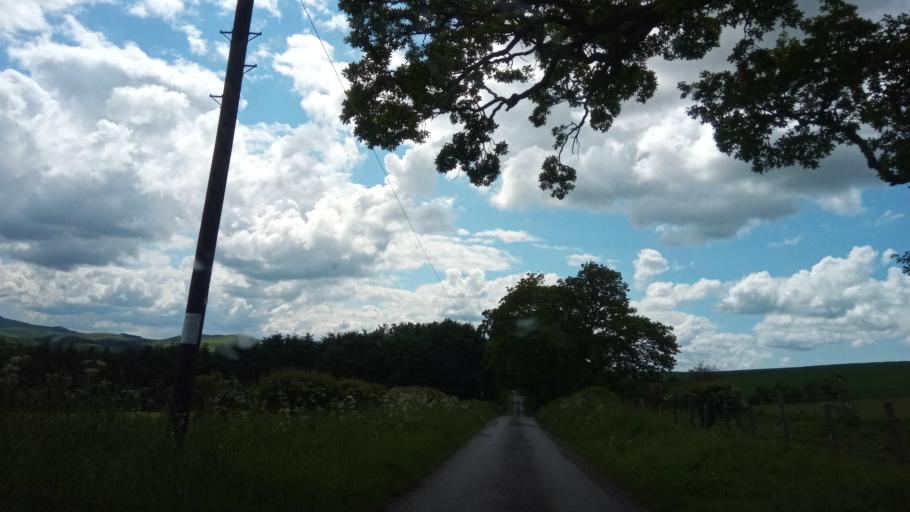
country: GB
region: Scotland
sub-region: The Scottish Borders
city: Coldstream
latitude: 55.5756
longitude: -2.3211
